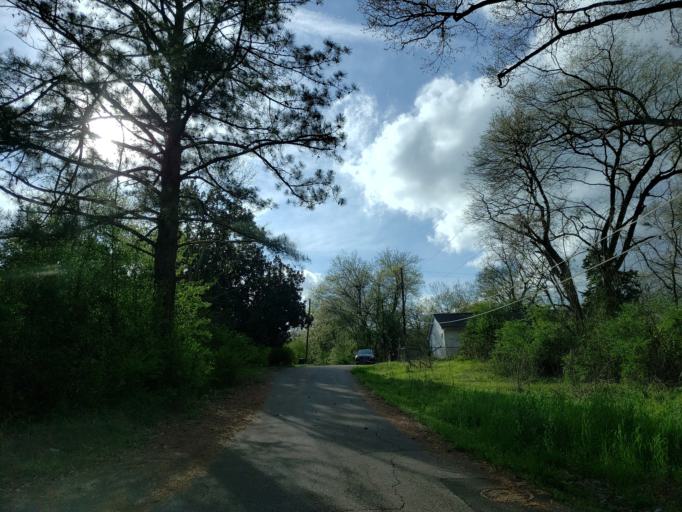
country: US
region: Georgia
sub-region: Bartow County
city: Emerson
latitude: 34.1258
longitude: -84.7602
